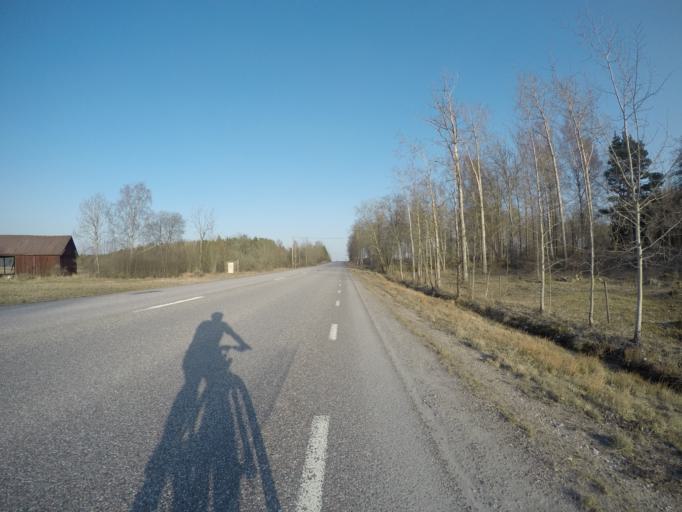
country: SE
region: Vaestmanland
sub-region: Kungsors Kommun
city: Kungsoer
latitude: 59.4204
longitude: 16.1538
